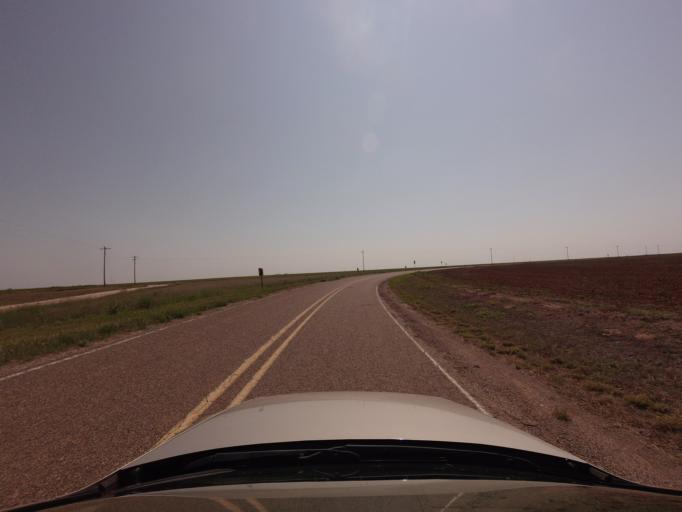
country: US
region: New Mexico
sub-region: Curry County
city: Cannon Air Force Base
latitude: 34.6325
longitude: -103.3034
